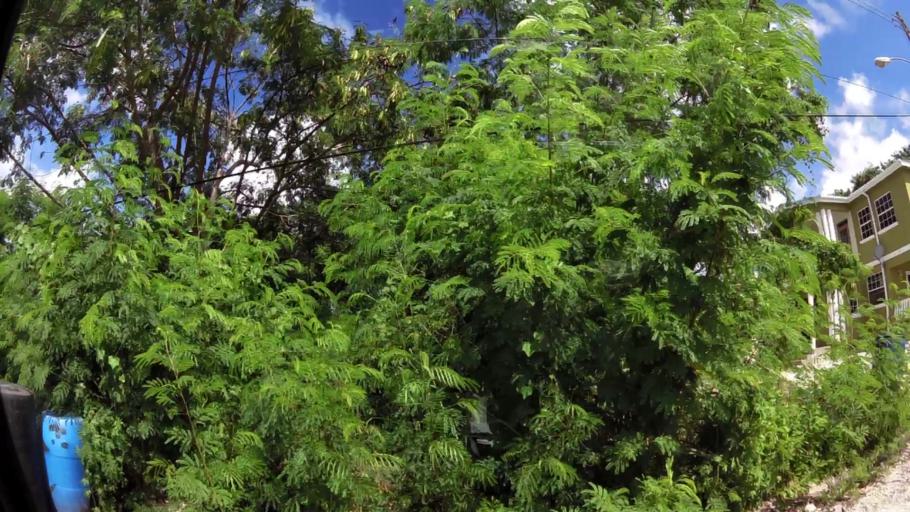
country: BB
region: Saint James
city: Holetown
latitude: 13.1538
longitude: -59.6339
